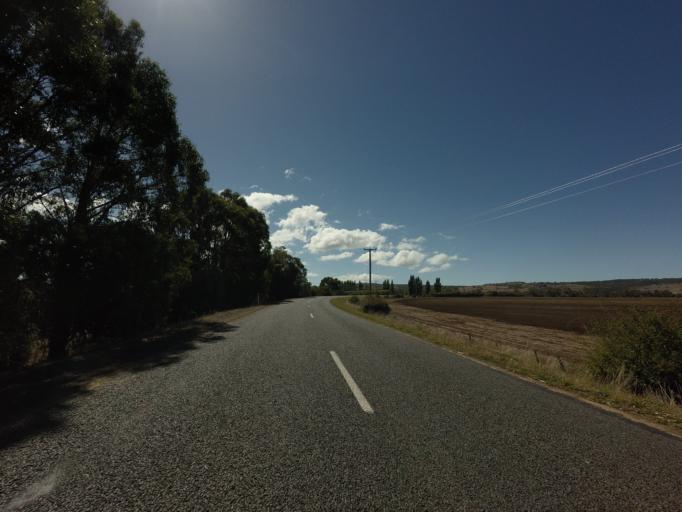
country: AU
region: Tasmania
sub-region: Break O'Day
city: St Helens
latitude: -41.9972
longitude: 148.0717
